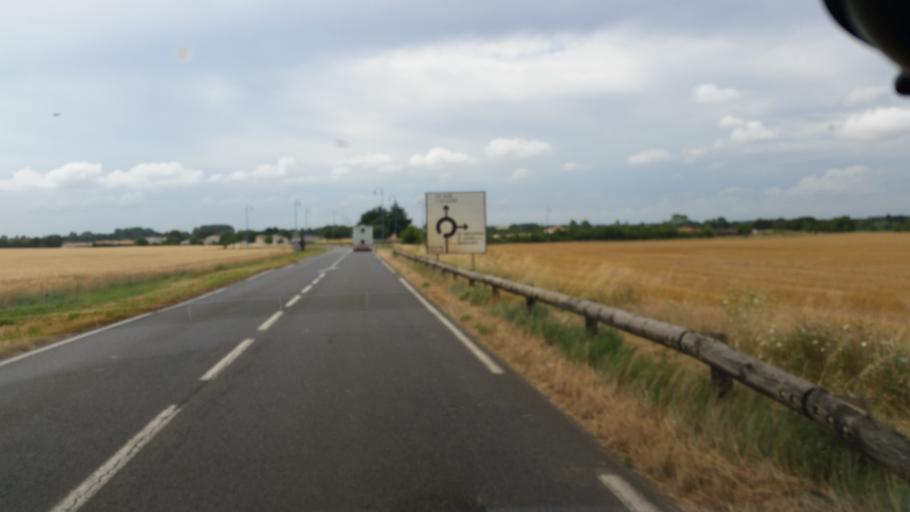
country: FR
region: Poitou-Charentes
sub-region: Departement de la Charente-Maritime
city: Courcon
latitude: 46.1817
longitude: -0.8537
